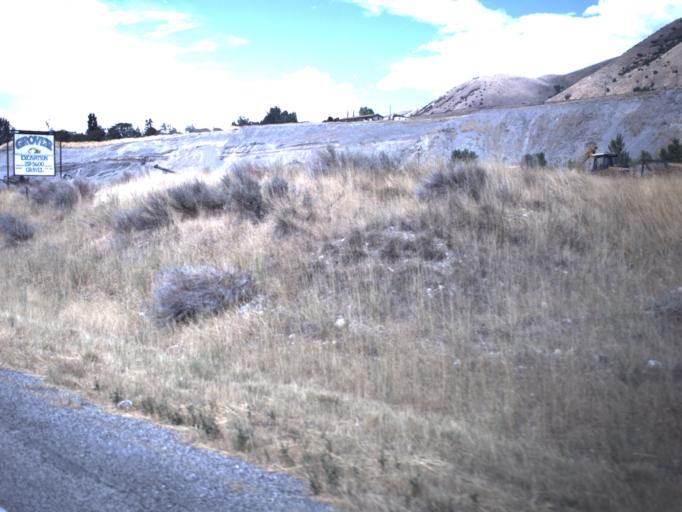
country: US
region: Utah
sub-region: Box Elder County
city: Elwood
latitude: 41.7312
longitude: -112.0982
